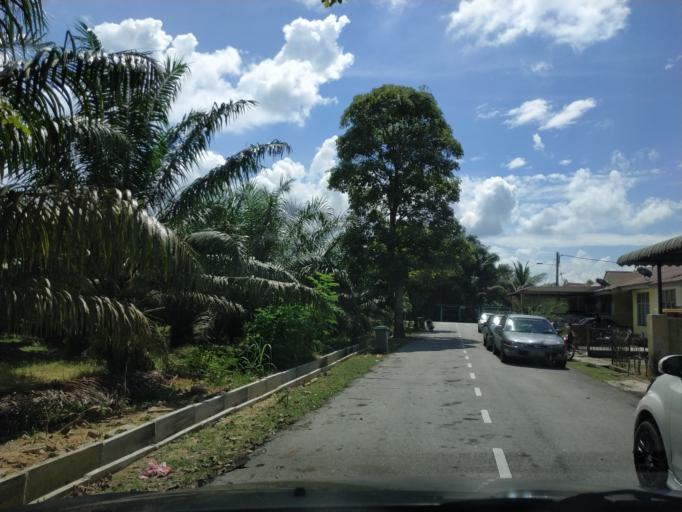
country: MY
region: Perak
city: Parit Buntar
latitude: 5.1391
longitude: 100.5973
